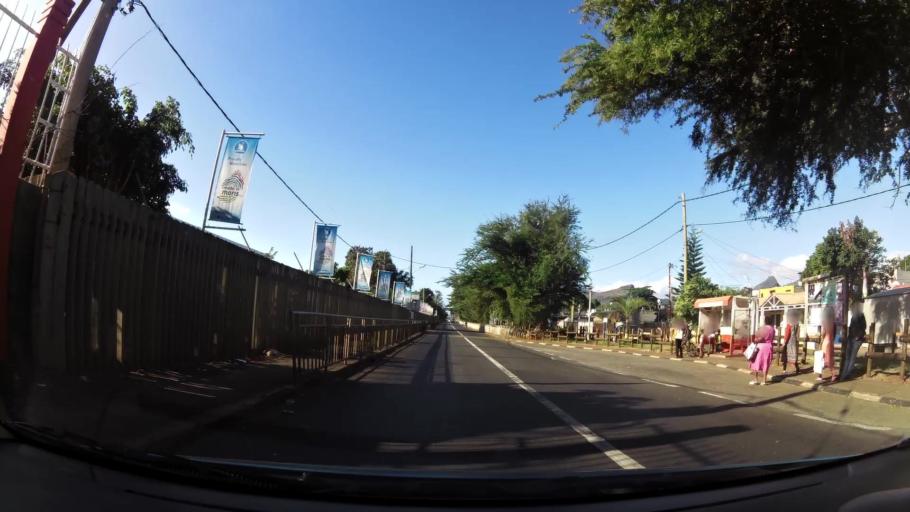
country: MU
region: Black River
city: Petite Riviere
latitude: -20.1877
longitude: 57.4578
